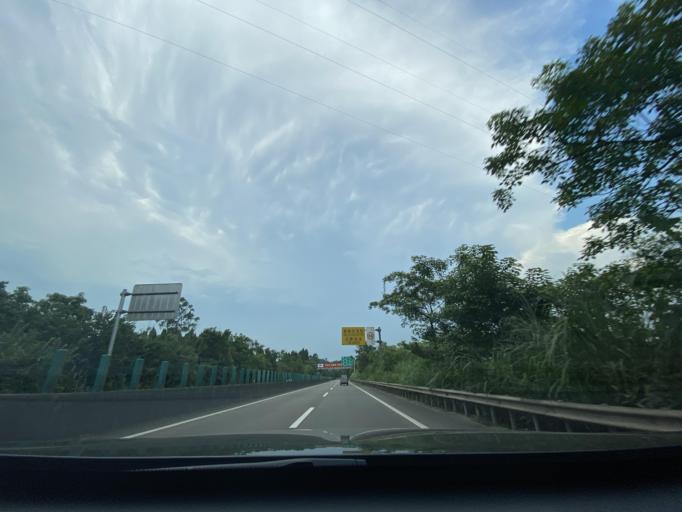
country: CN
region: Sichuan
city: Neijiang
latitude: 29.6296
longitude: 104.9846
